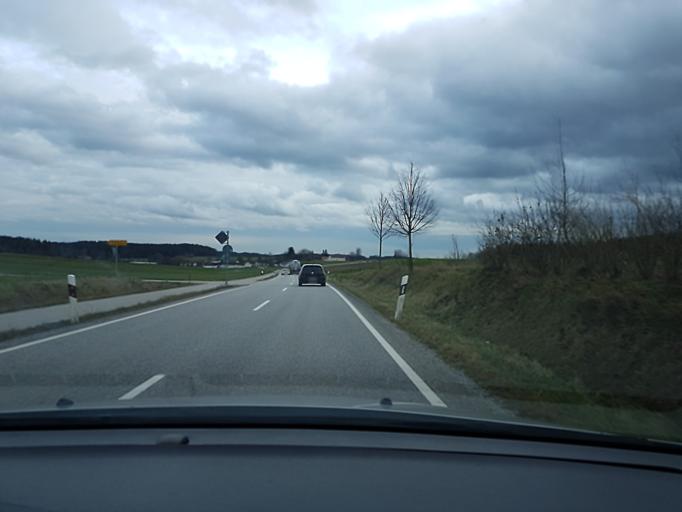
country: DE
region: Bavaria
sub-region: Lower Bavaria
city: Furth
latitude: 48.4180
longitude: 12.3652
